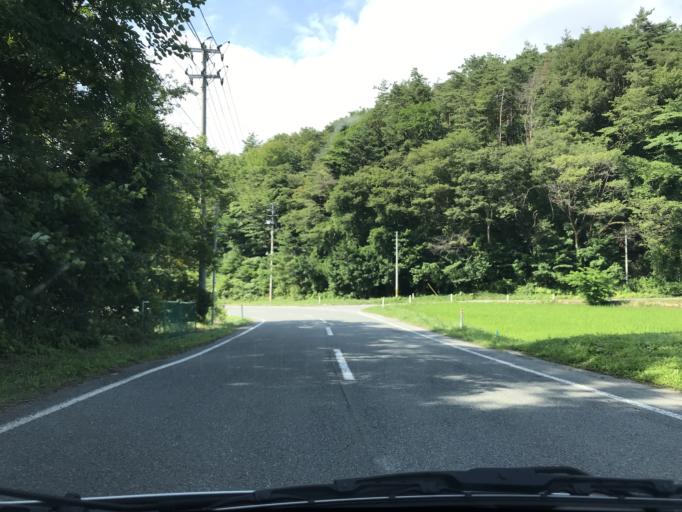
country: JP
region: Iwate
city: Ichinoseki
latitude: 39.0055
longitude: 141.2670
